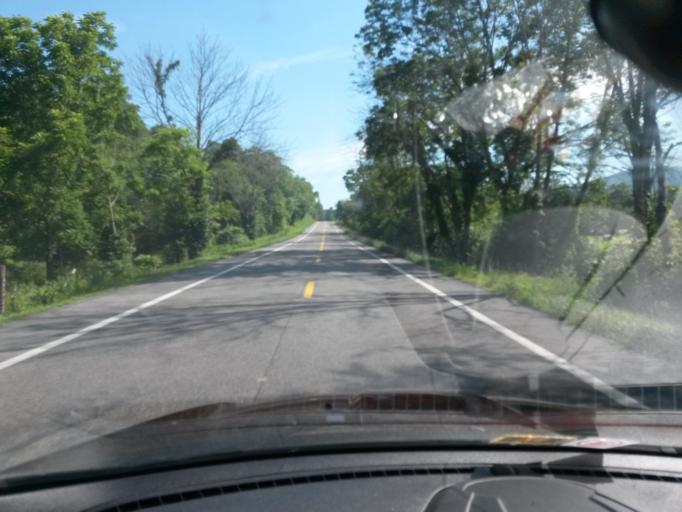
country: US
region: Virginia
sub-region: Shenandoah County
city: Basye
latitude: 38.8041
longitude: -78.8886
